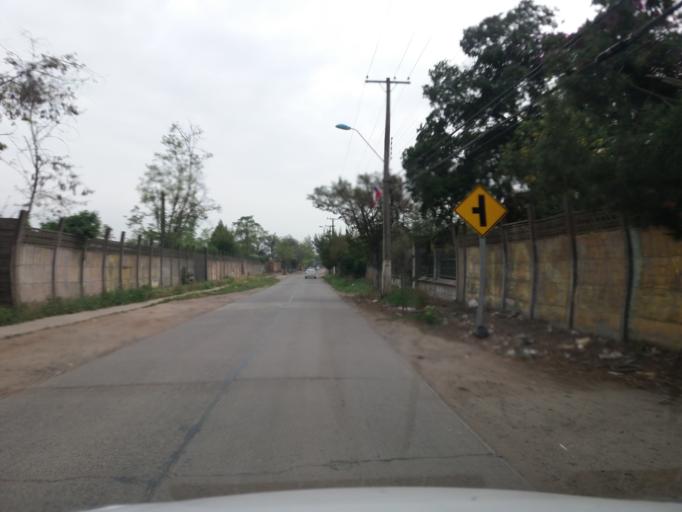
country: CL
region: Valparaiso
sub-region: Provincia de Quillota
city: Hacienda La Calera
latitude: -32.8230
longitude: -71.1306
